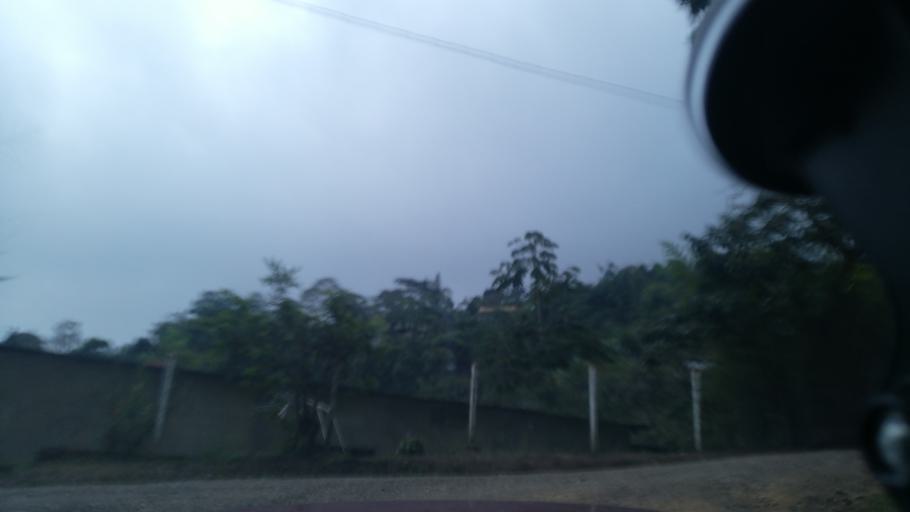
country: CO
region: Cundinamarca
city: San Antonio del Tequendama
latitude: 4.6643
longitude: -74.3997
